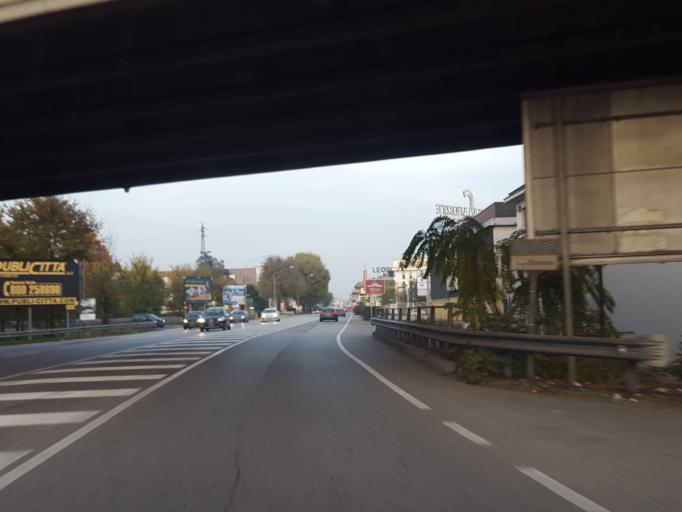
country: IT
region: Veneto
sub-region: Provincia di Vicenza
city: Creazzo
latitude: 45.5344
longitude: 11.5078
